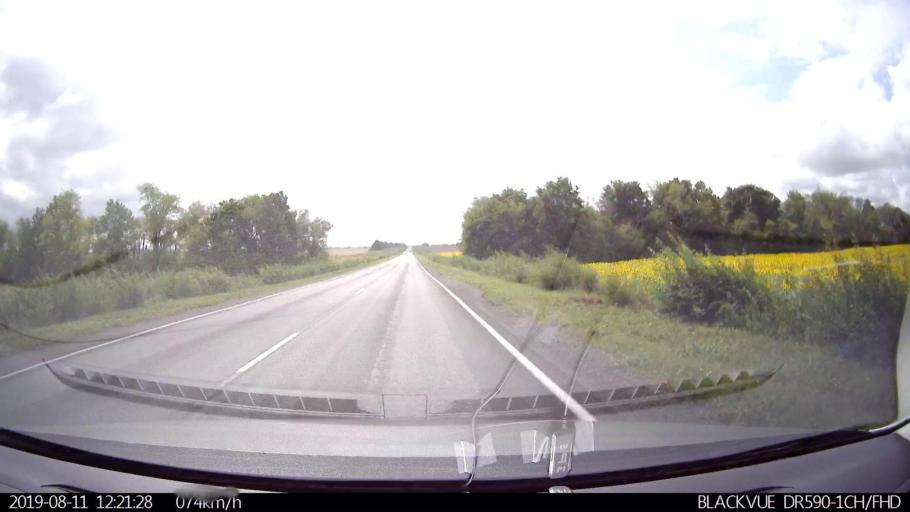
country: RU
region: Ulyanovsk
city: Ignatovka
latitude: 53.9204
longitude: 47.9577
